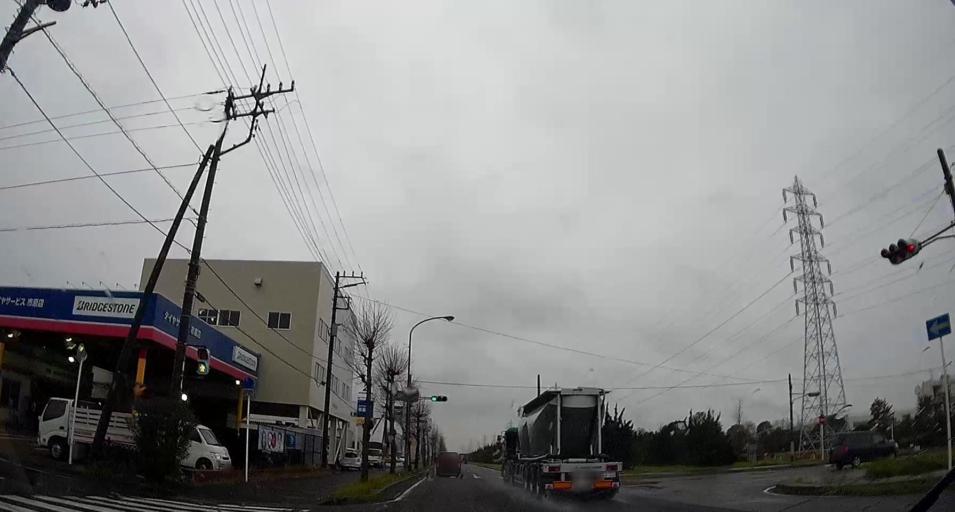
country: JP
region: Chiba
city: Ichihara
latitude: 35.5002
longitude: 140.0492
